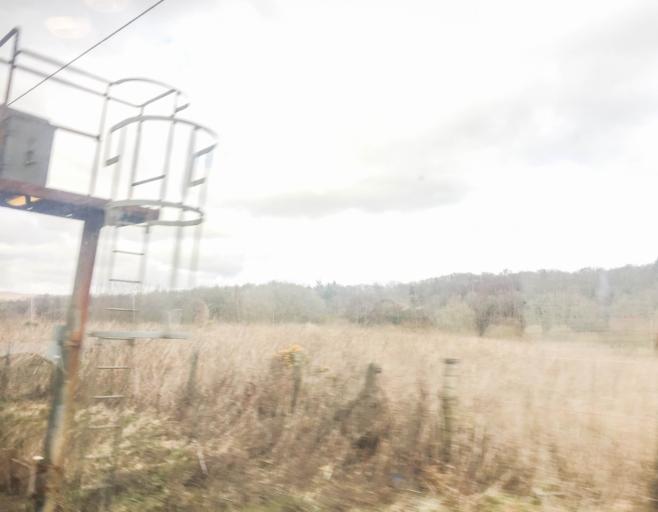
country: GB
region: Scotland
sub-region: Argyll and Bute
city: Helensburgh
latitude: 55.9889
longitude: -4.6967
